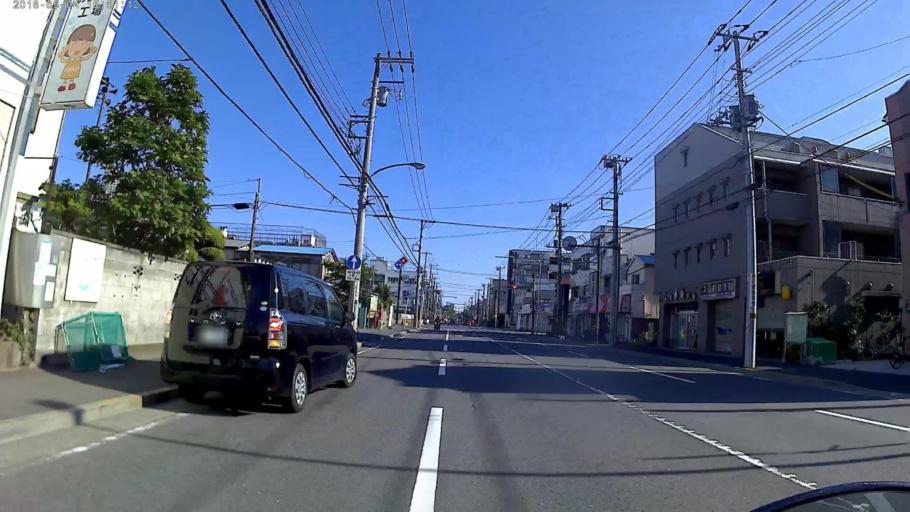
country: JP
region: Kanagawa
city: Yokohama
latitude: 35.4914
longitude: 139.6483
